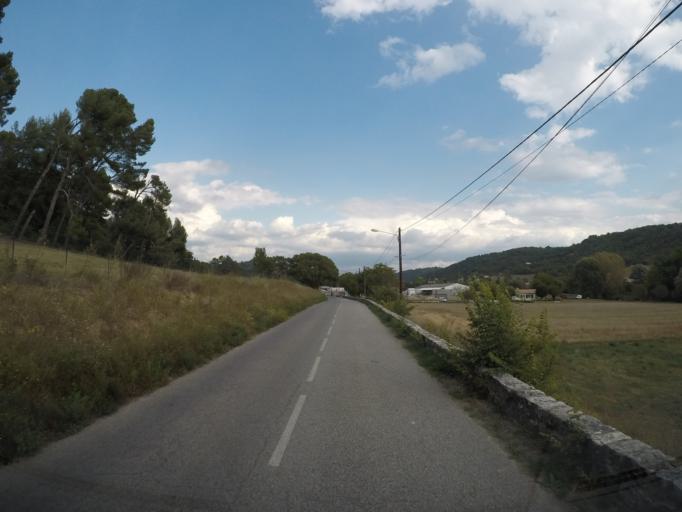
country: FR
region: Provence-Alpes-Cote d'Azur
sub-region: Departement des Alpes-de-Haute-Provence
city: Riez
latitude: 43.8162
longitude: 6.0765
